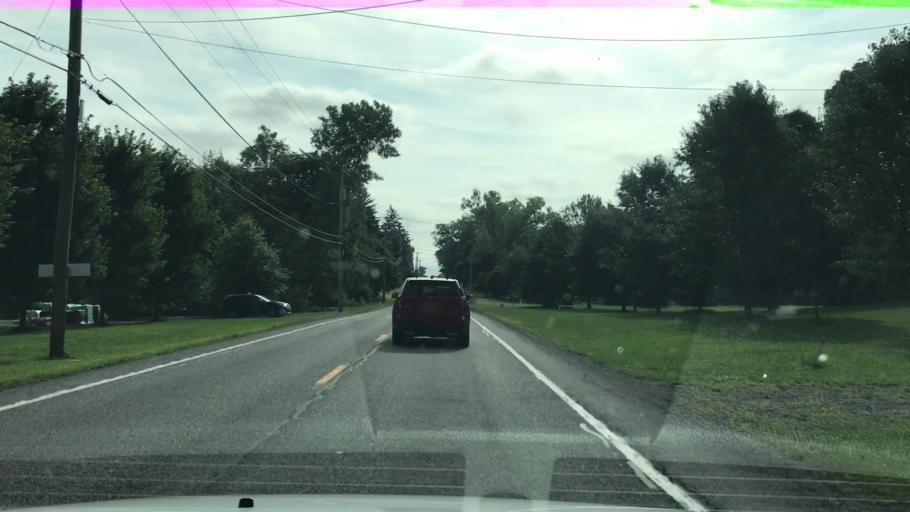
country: US
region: New York
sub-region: Erie County
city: Town Line
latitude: 42.8564
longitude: -78.5700
